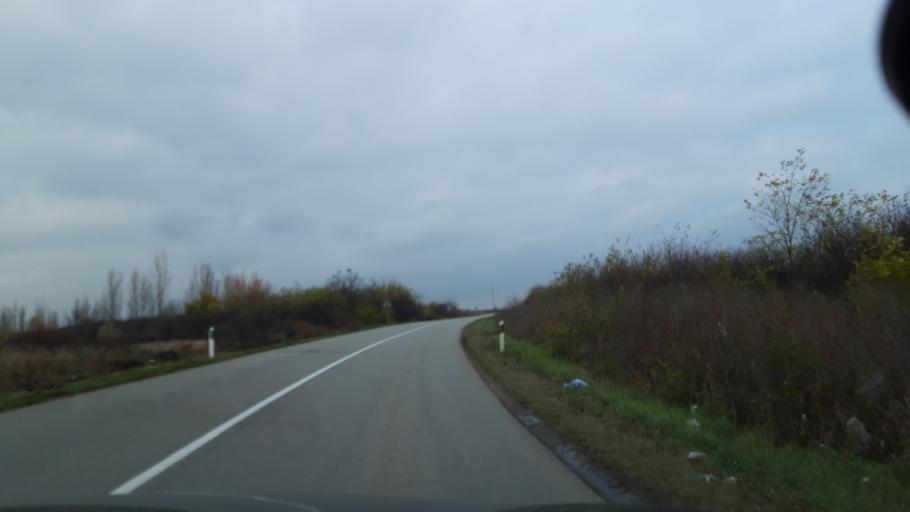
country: RS
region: Autonomna Pokrajina Vojvodina
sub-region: Severnobanatski Okrug
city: Novi Knezevac
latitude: 46.0762
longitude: 20.1033
